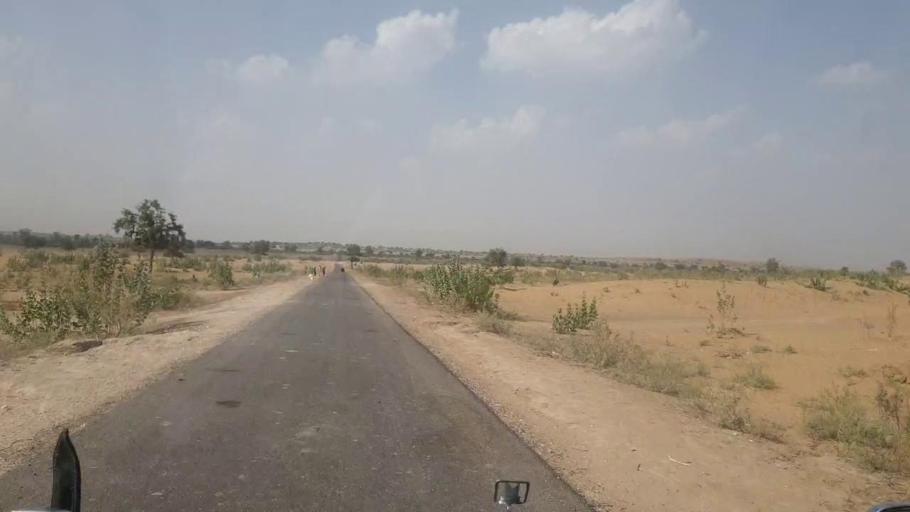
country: PK
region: Sindh
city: Islamkot
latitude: 25.2204
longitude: 70.2888
